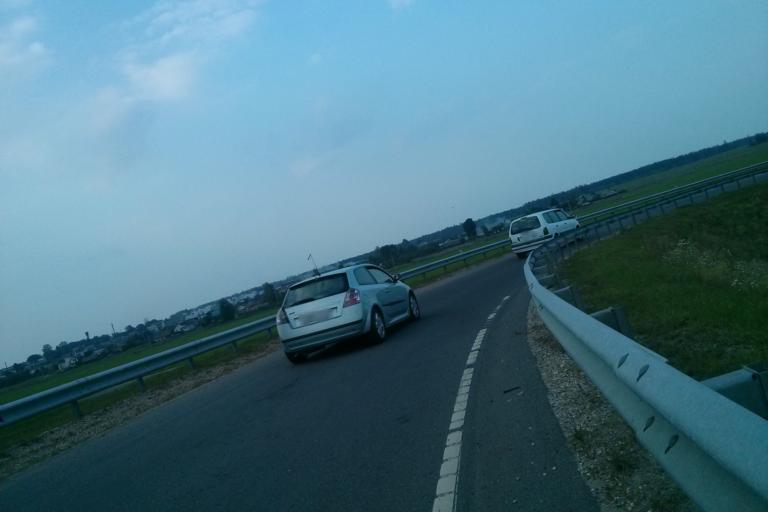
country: BY
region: Minsk
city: Chervyen'
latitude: 53.7251
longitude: 28.3937
